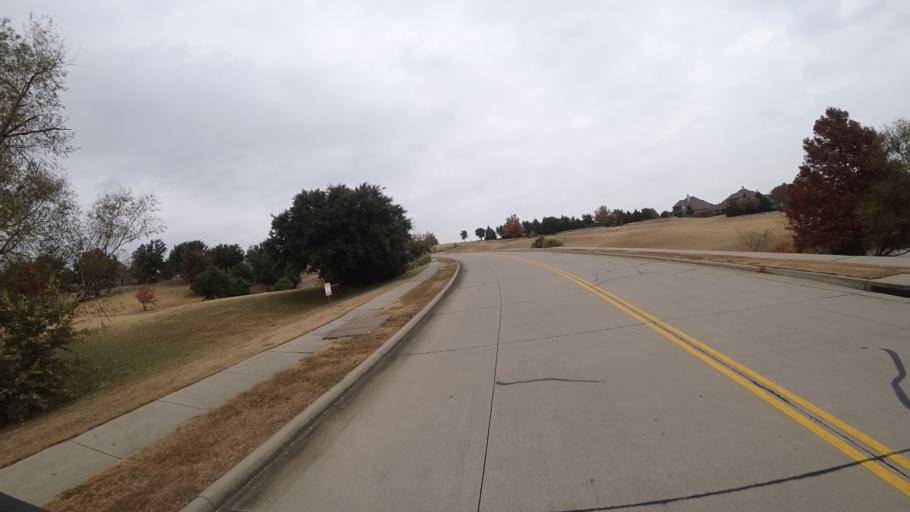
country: US
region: Texas
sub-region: Denton County
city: Lewisville
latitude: 33.0291
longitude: -96.9332
